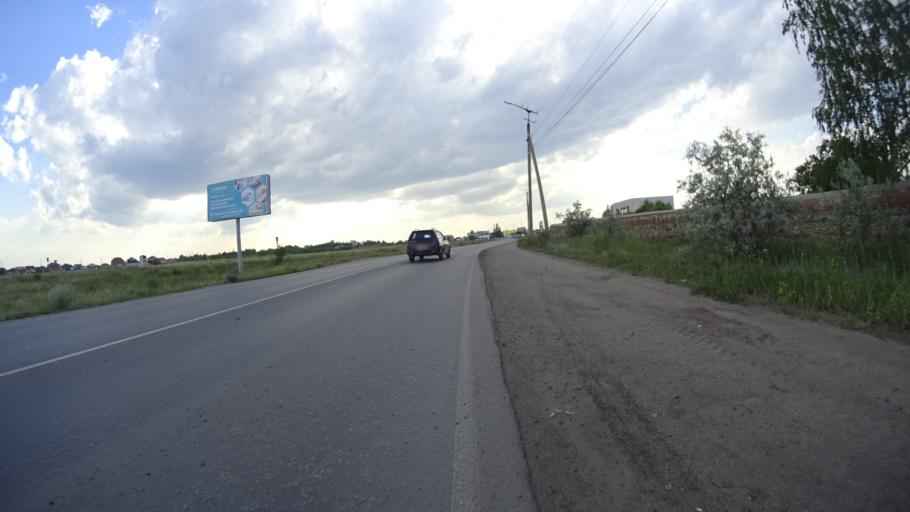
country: RU
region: Chelyabinsk
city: Troitsk
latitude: 54.0814
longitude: 61.5216
